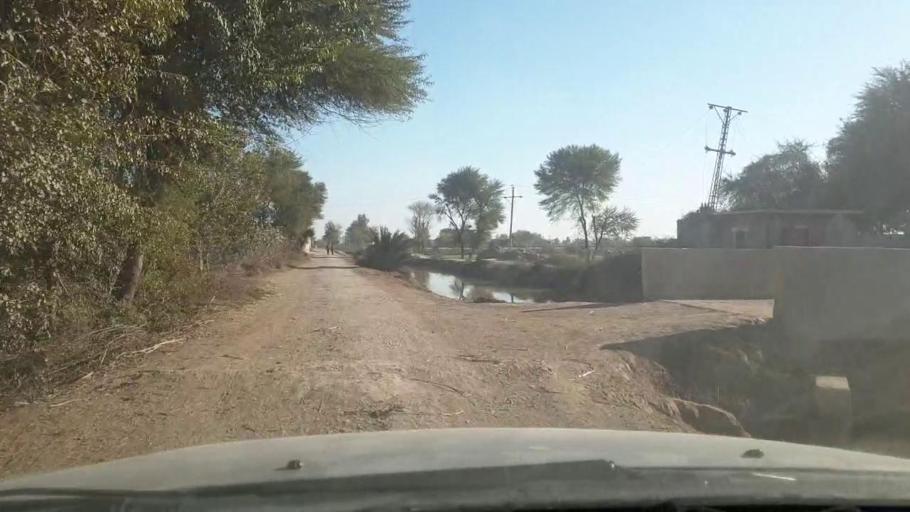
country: PK
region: Sindh
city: Adilpur
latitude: 27.9415
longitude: 69.2204
